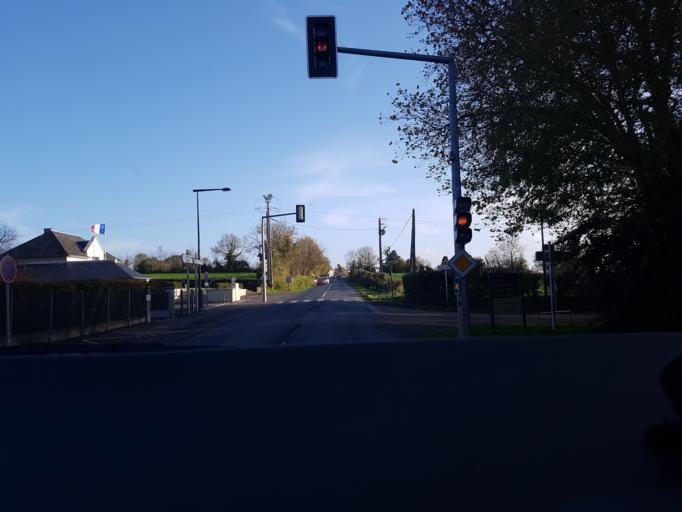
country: FR
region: Lower Normandy
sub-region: Departement du Calvados
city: Port-en-Bessin-Huppain
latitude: 49.3181
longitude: -0.7452
